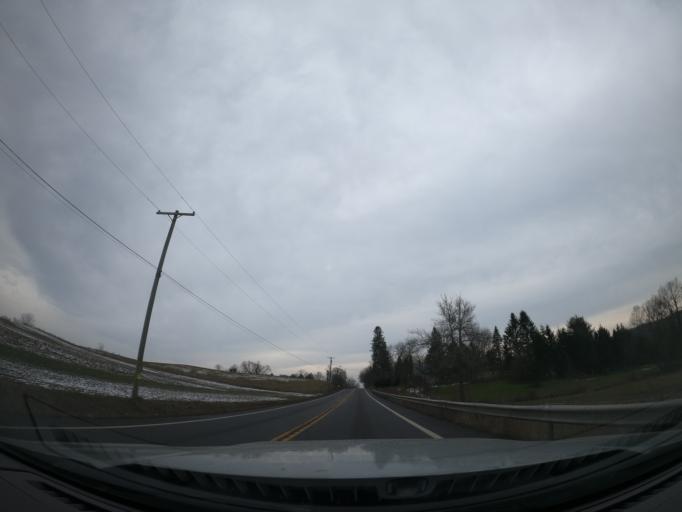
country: US
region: New York
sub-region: Cayuga County
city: Moravia
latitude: 42.7086
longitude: -76.5410
